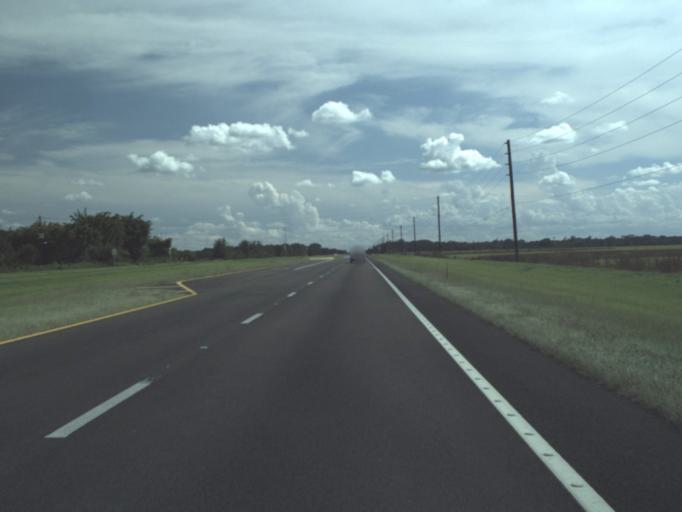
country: US
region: Florida
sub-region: Hardee County
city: Zolfo Springs
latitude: 27.4401
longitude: -81.7966
